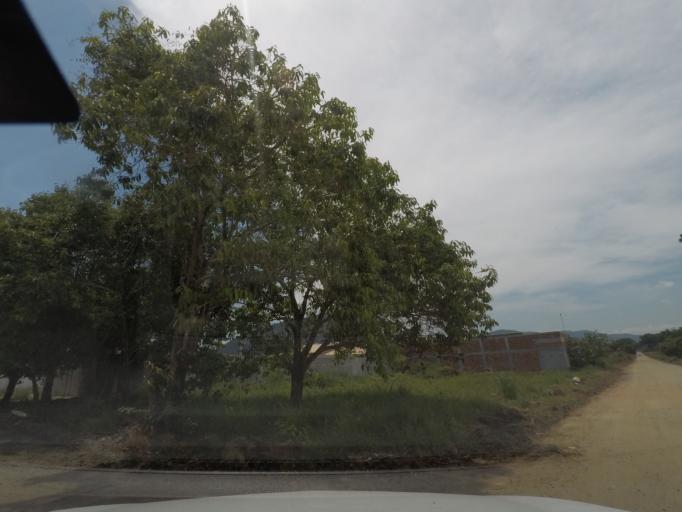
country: BR
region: Rio de Janeiro
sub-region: Marica
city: Marica
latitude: -22.9544
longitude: -42.9456
